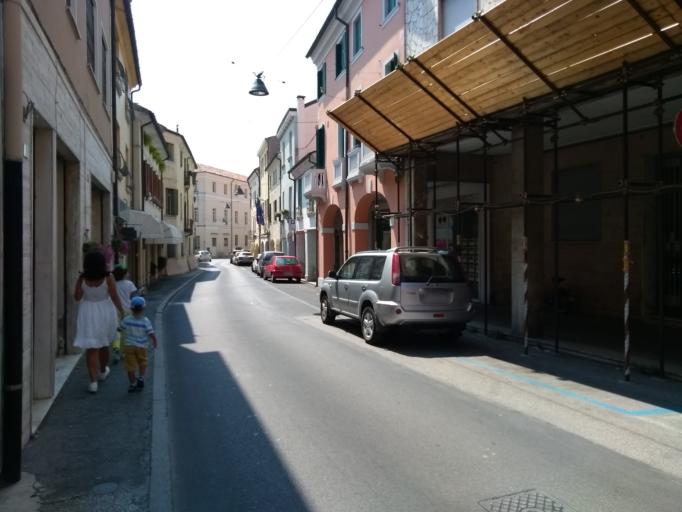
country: IT
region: Veneto
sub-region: Provincia di Rovigo
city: Rovigo
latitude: 45.0693
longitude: 11.7887
